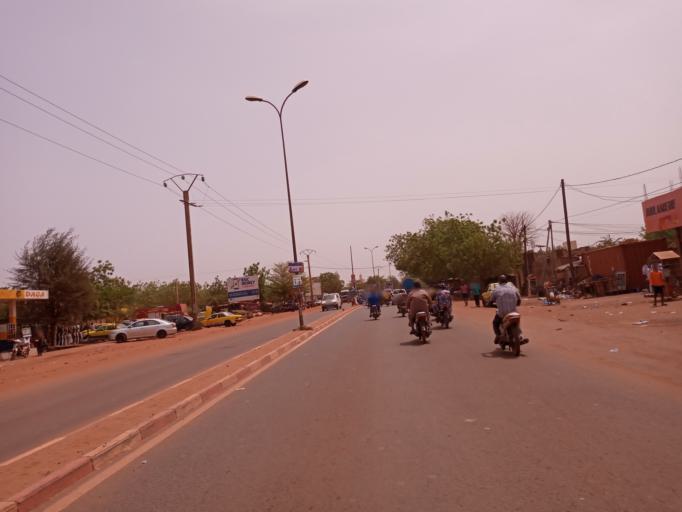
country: ML
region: Bamako
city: Bamako
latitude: 12.6701
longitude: -7.9219
